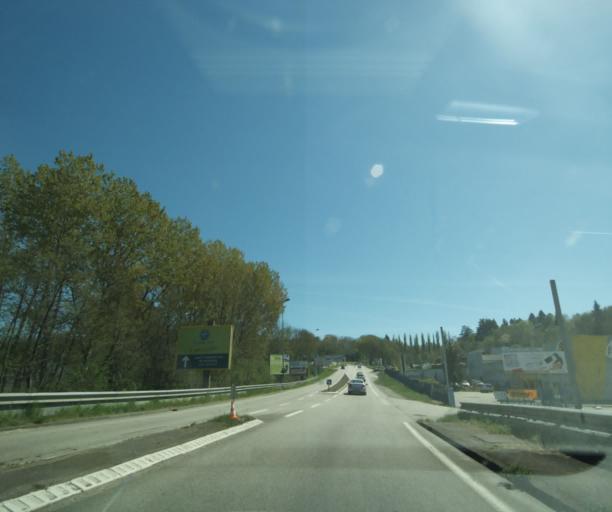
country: FR
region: Limousin
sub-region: Departement de la Haute-Vienne
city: Condat-sur-Vienne
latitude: 45.8034
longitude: 1.2922
